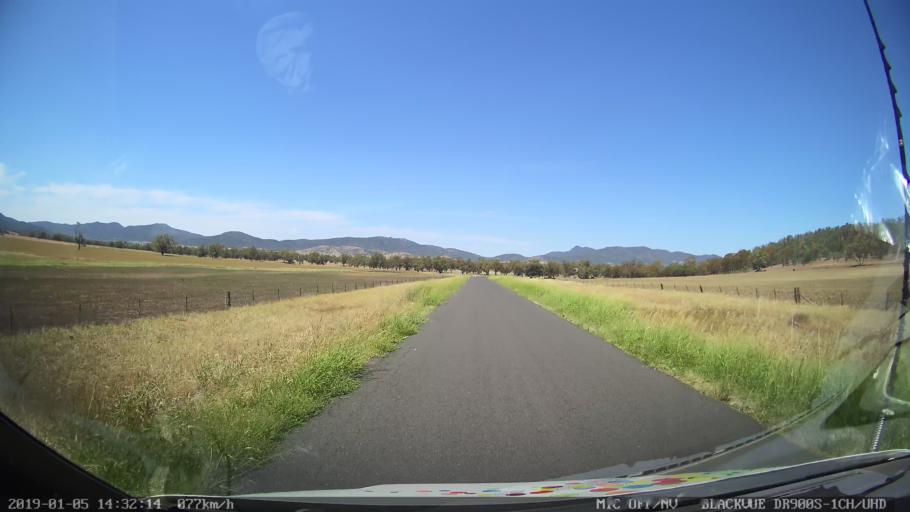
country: AU
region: New South Wales
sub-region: Tamworth Municipality
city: Phillip
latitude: -31.2216
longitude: 150.6156
